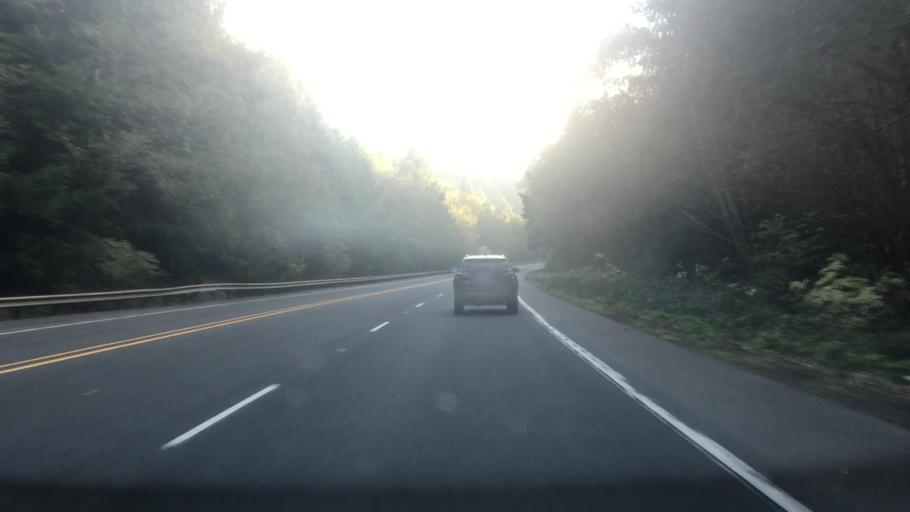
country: US
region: Oregon
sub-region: Clatsop County
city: Cannon Beach
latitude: 45.9254
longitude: -123.9306
